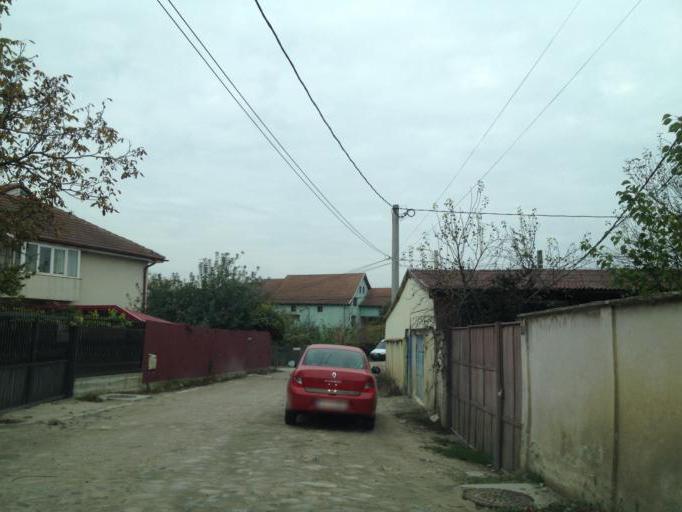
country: RO
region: Dolj
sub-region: Municipiul Craiova
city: Facai
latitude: 44.2926
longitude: 23.8078
